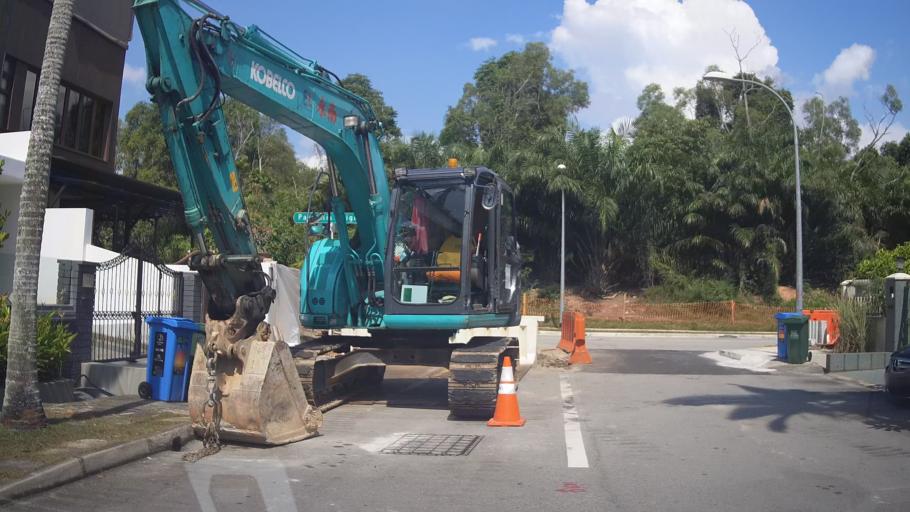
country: MY
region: Johor
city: Kampung Pasir Gudang Baru
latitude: 1.3826
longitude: 103.9428
